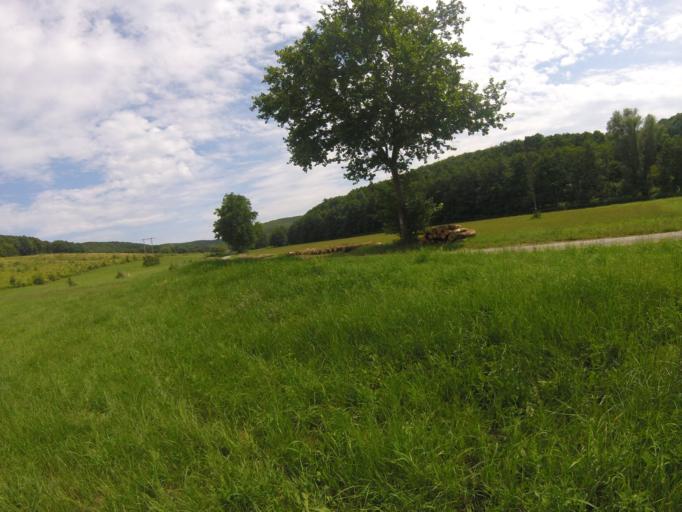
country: HU
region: Zala
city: Lenti
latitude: 46.5636
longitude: 16.6336
